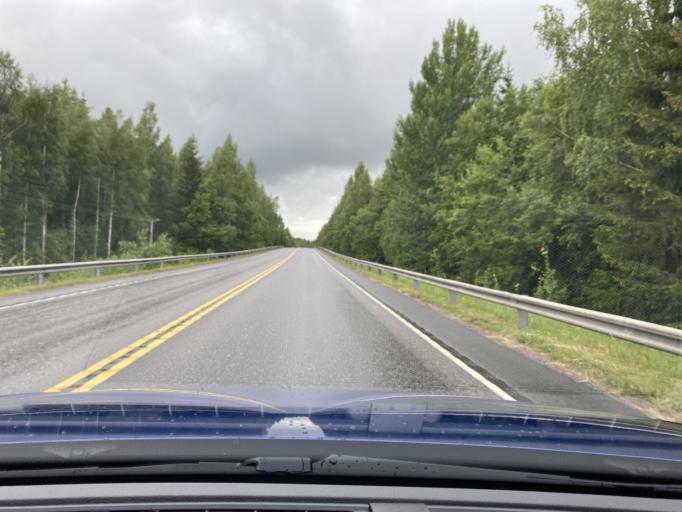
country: FI
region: Uusimaa
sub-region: Helsinki
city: Hyvinge
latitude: 60.5701
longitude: 24.8055
